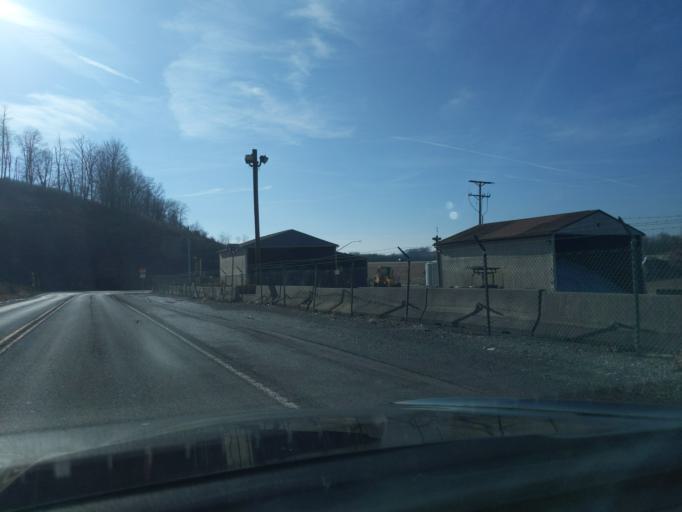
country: US
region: Pennsylvania
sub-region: Blair County
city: Bellwood
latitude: 40.5993
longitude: -78.3126
